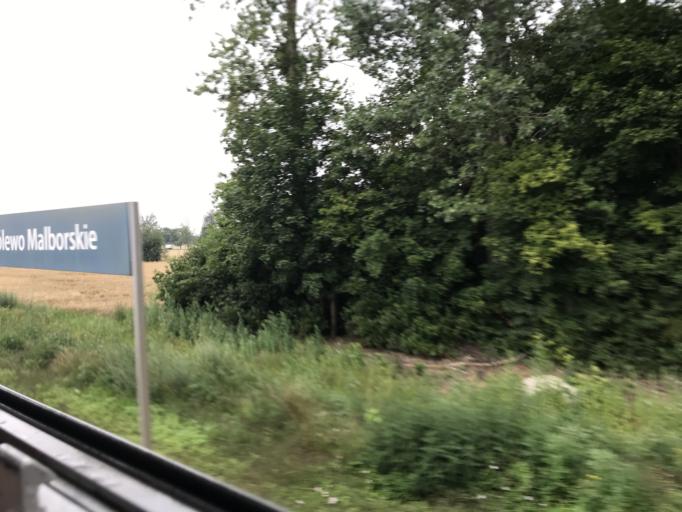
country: PL
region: Pomeranian Voivodeship
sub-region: Powiat malborski
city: Malbork
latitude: 54.0371
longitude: 19.1173
